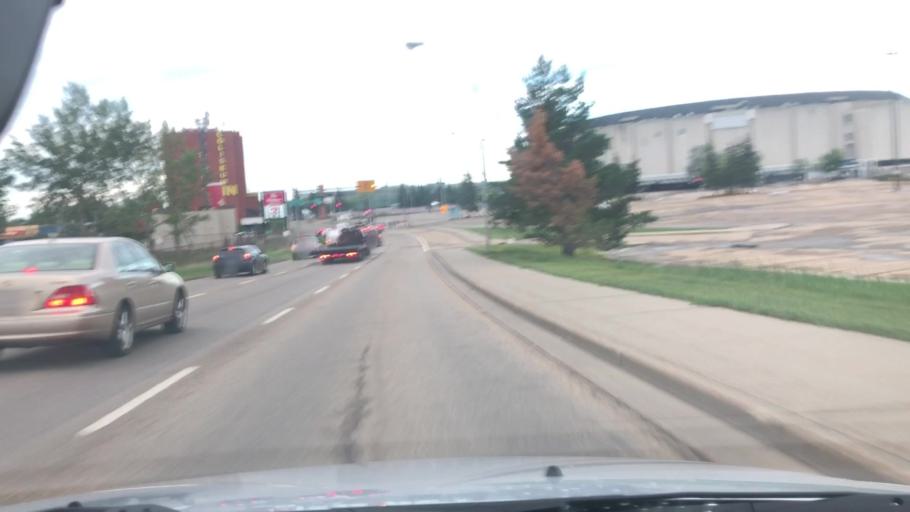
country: CA
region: Alberta
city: Edmonton
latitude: 53.5736
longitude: -113.4533
